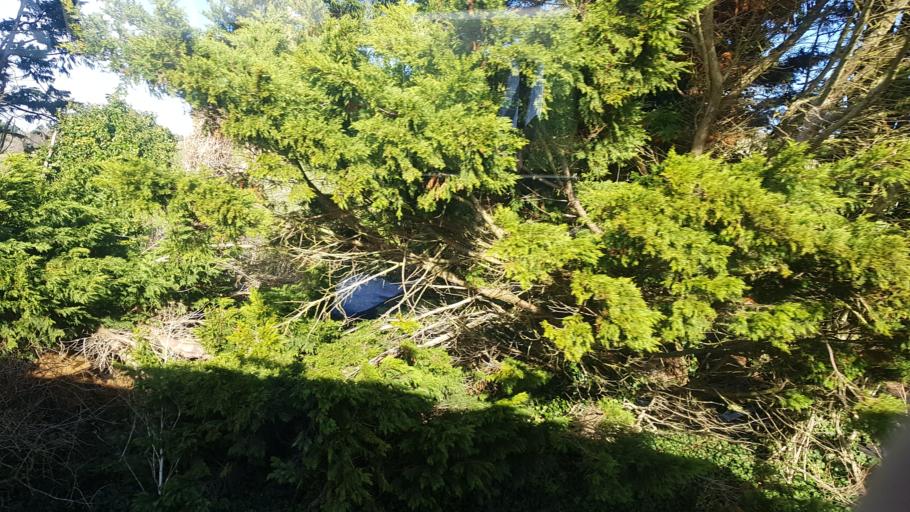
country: GB
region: England
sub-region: Isle of Wight
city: Shalfleet
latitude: 50.6421
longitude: -1.3785
